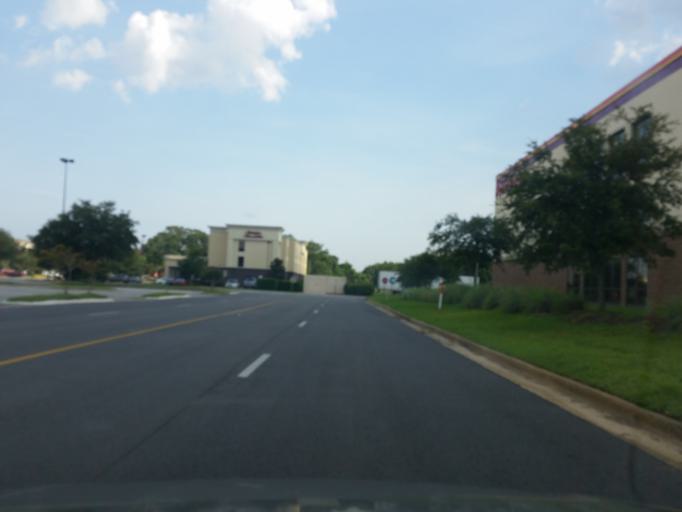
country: US
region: Florida
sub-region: Escambia County
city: Ferry Pass
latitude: 30.4985
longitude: -87.2265
